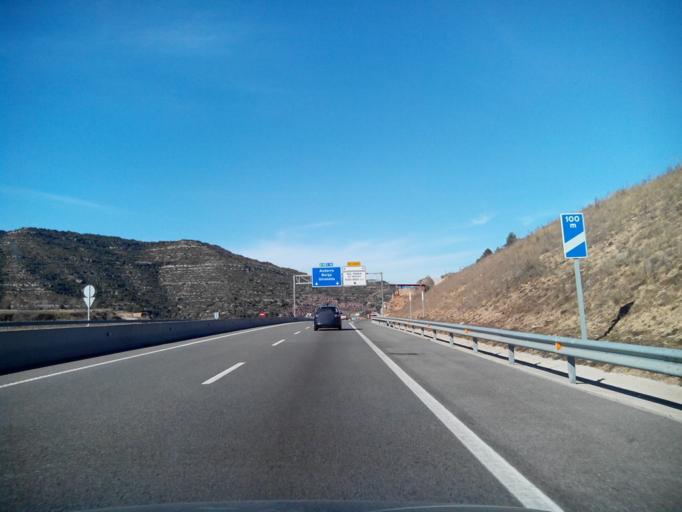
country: ES
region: Catalonia
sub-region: Provincia de Barcelona
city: Puig-reig
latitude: 41.9760
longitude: 1.8882
